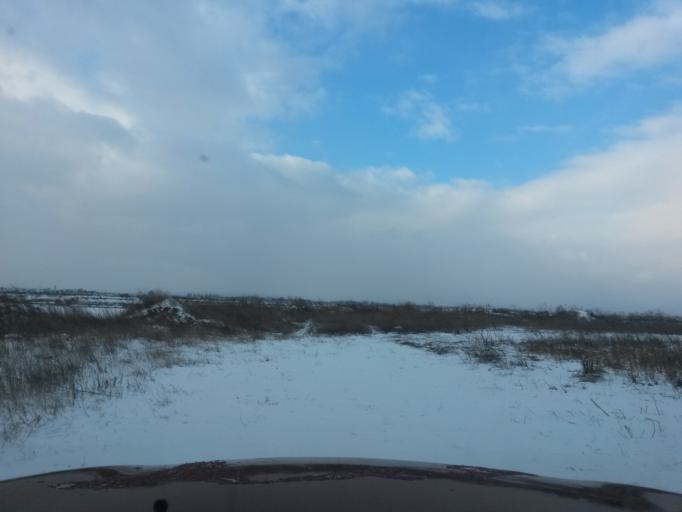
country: SK
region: Kosicky
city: Kosice
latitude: 48.6293
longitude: 21.3373
